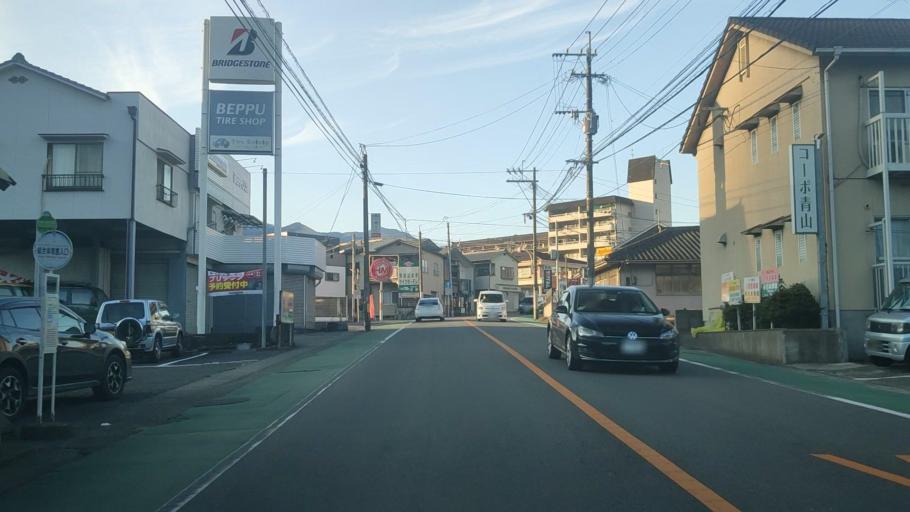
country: JP
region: Oita
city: Beppu
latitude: 33.2774
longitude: 131.4901
